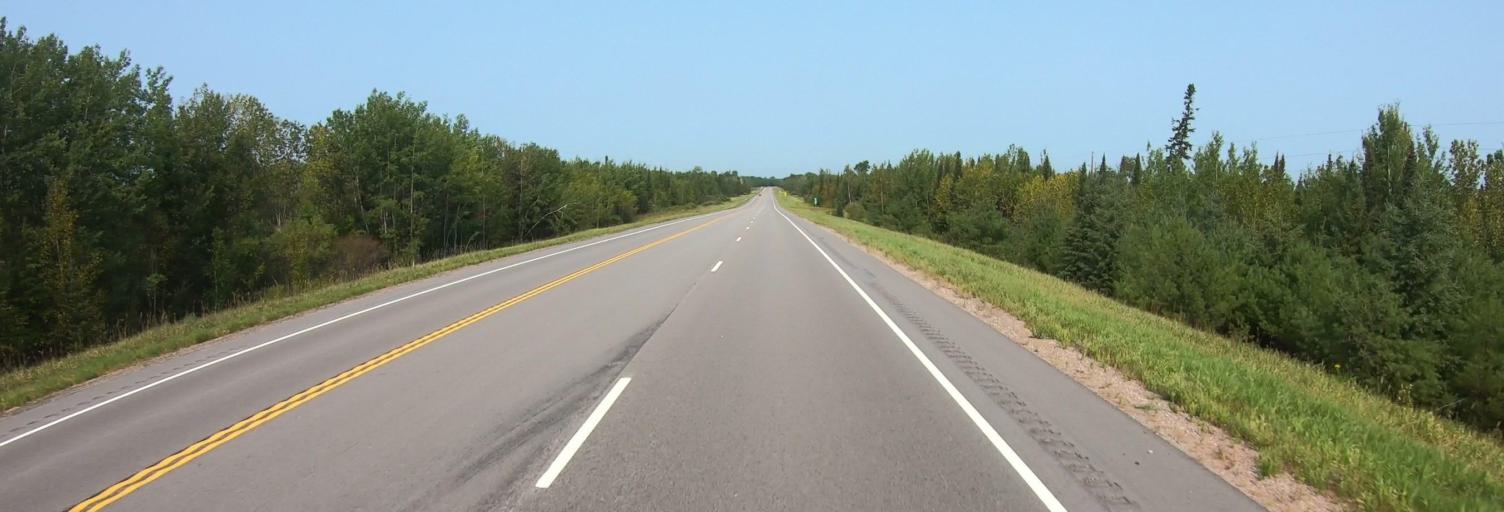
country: US
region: Minnesota
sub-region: Saint Louis County
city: Mountain Iron
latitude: 47.9160
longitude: -92.8101
